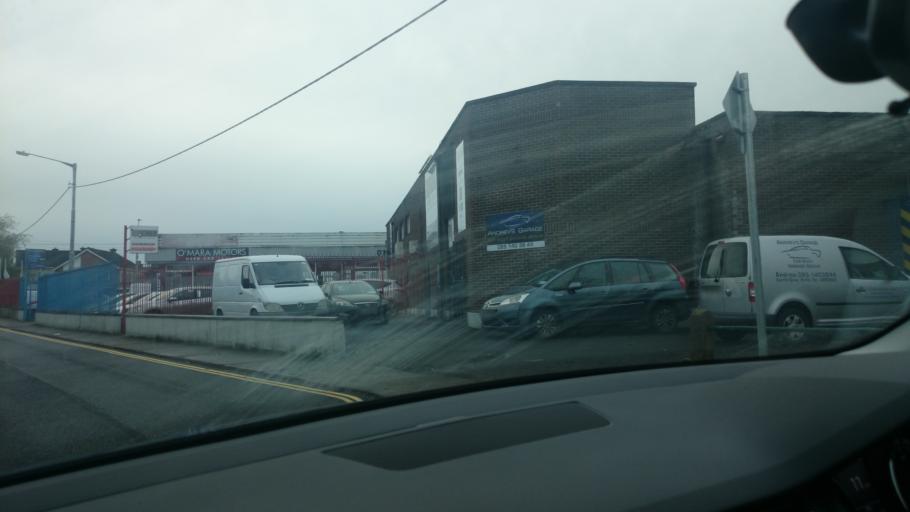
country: IE
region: Munster
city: Moyross
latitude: 52.6706
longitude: -8.6565
